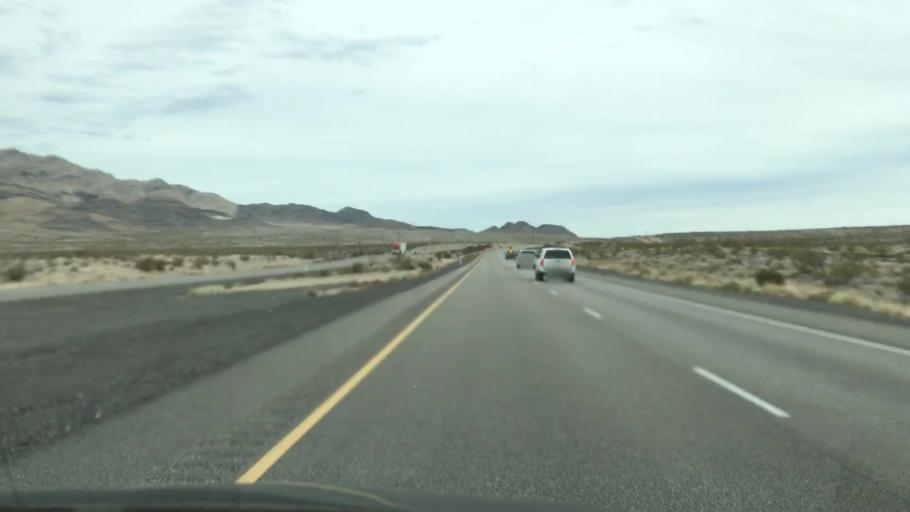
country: US
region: Nevada
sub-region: Nye County
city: Pahrump
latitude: 36.6003
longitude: -115.9848
